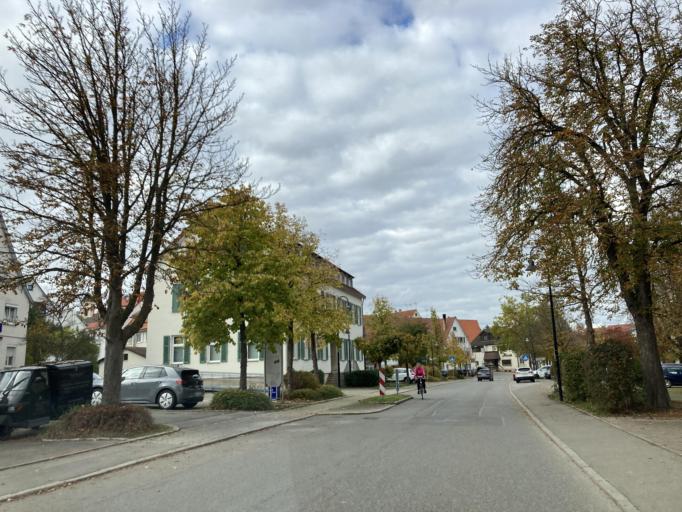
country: DE
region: Baden-Wuerttemberg
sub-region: Tuebingen Region
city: Dusslingen
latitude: 48.4511
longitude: 9.0552
